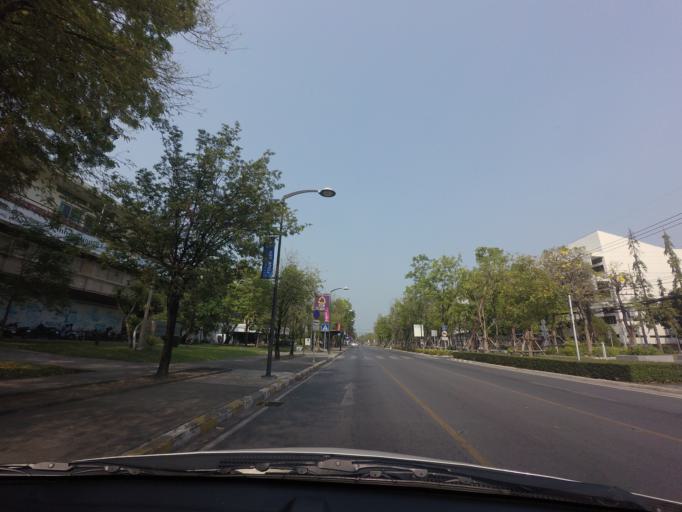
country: TH
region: Bangkok
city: Thawi Watthana
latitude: 13.7918
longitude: 100.3242
